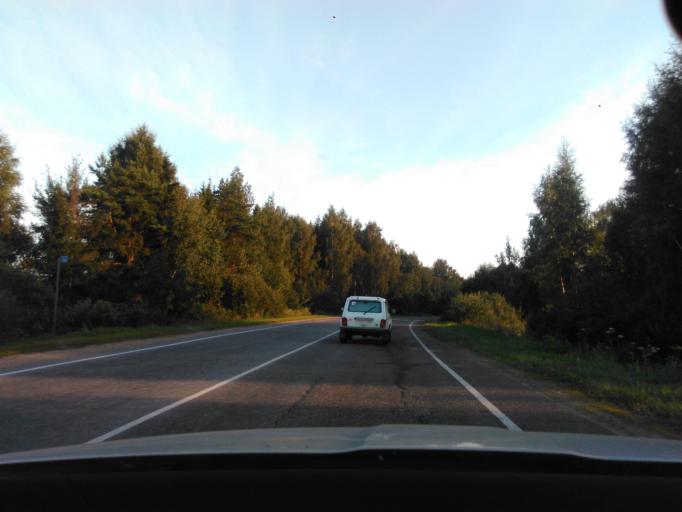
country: RU
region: Tverskaya
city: Konakovo
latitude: 56.6568
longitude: 36.7146
